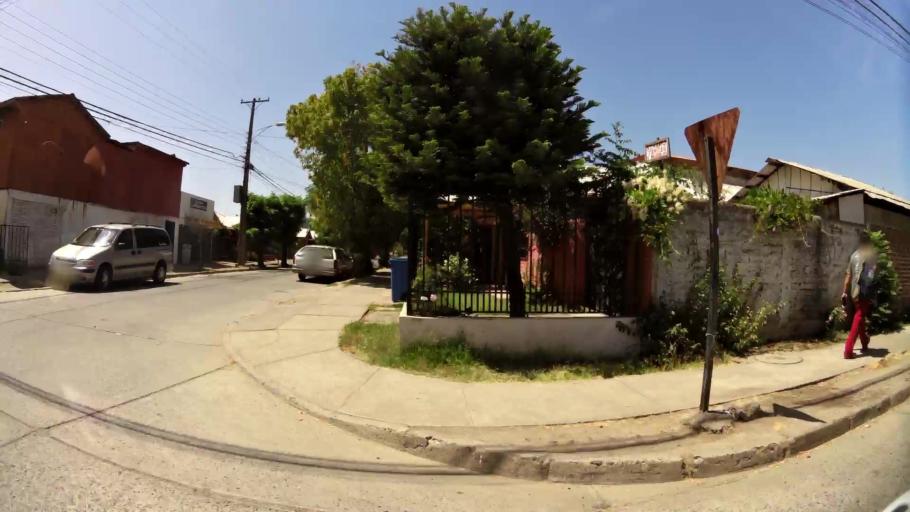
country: CL
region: Maule
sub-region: Provincia de Talca
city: Talca
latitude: -35.4292
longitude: -71.6313
